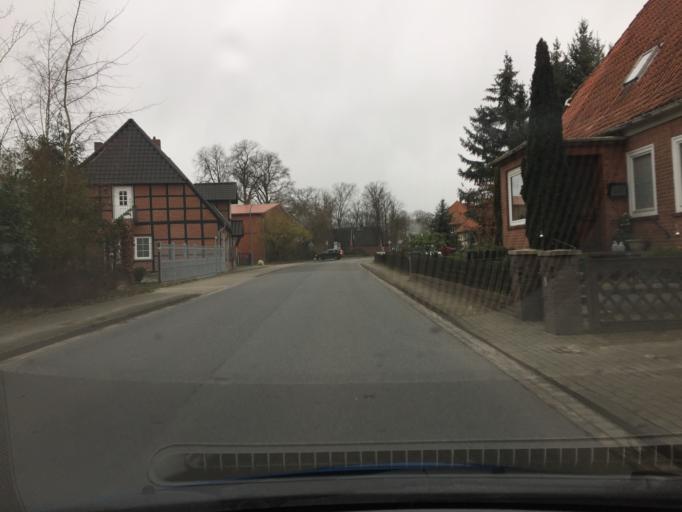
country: DE
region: Lower Saxony
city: Emmendorf
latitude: 53.0059
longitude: 10.6081
